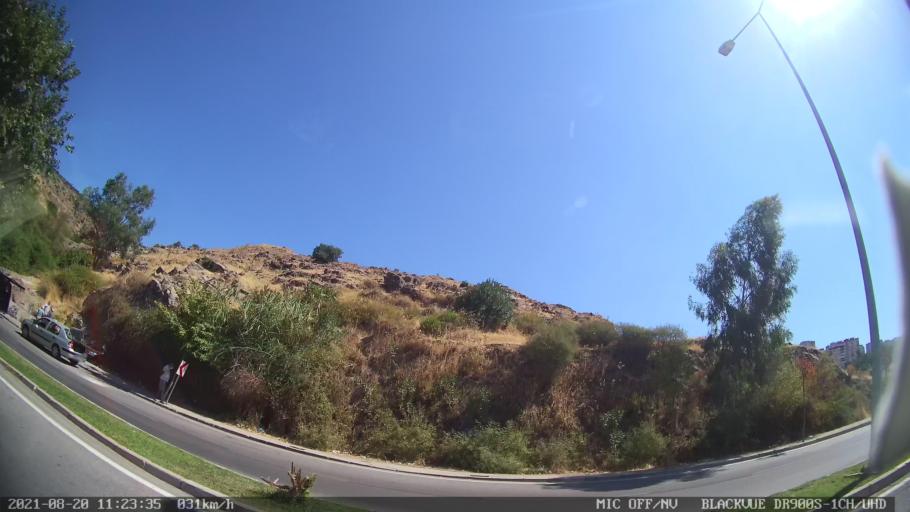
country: TR
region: Izmir
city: Karsiyaka
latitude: 38.5049
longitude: 27.0823
